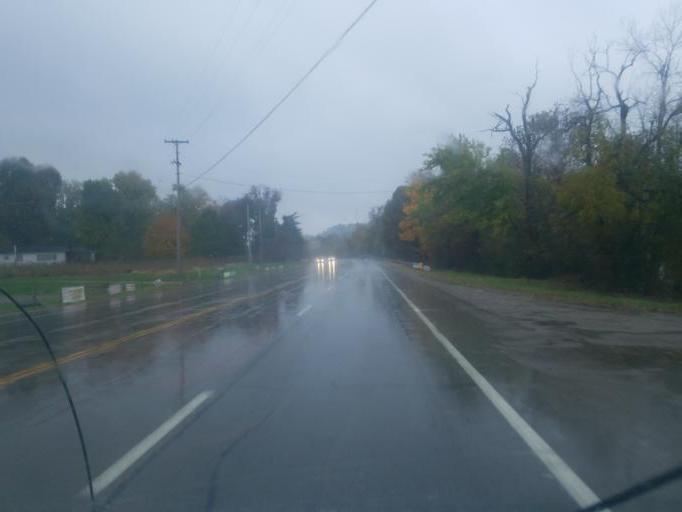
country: US
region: Ohio
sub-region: Muskingum County
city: South Zanesville
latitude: 39.9004
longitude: -82.0002
